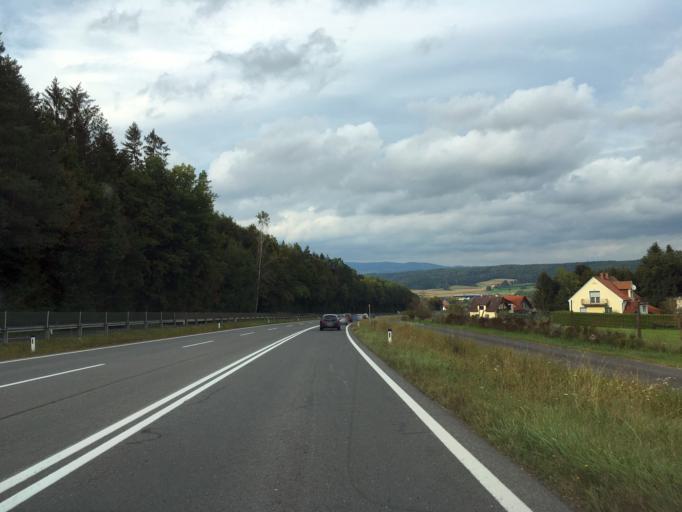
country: AT
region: Styria
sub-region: Politischer Bezirk Hartberg-Fuerstenfeld
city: Lafnitz
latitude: 47.3576
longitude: 16.0115
